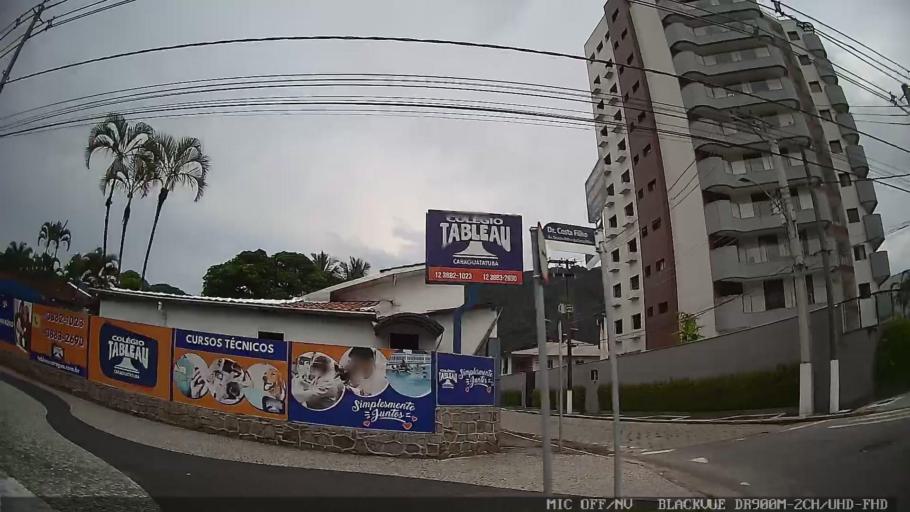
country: BR
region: Sao Paulo
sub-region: Caraguatatuba
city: Caraguatatuba
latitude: -23.6222
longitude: -45.4057
